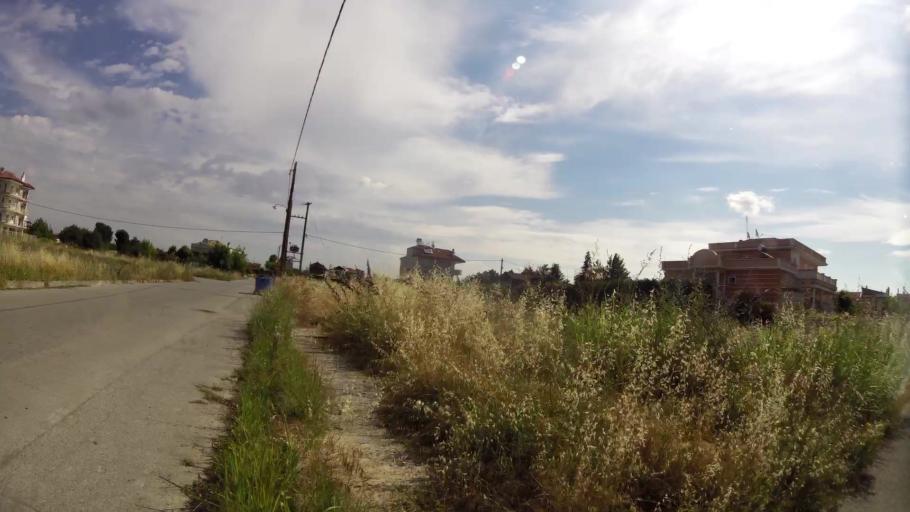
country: GR
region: Central Macedonia
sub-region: Nomos Pierias
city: Katerini
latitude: 40.2812
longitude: 22.4959
